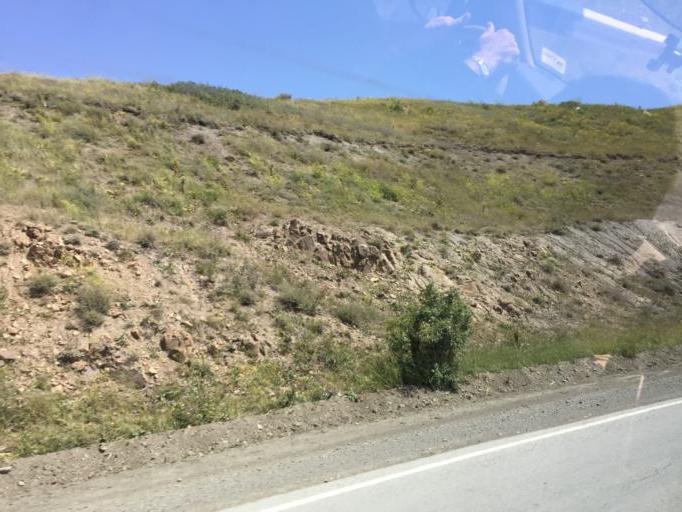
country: AM
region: Vayots' Dzori Marz
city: Jermuk
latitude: 39.6911
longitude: 45.7006
